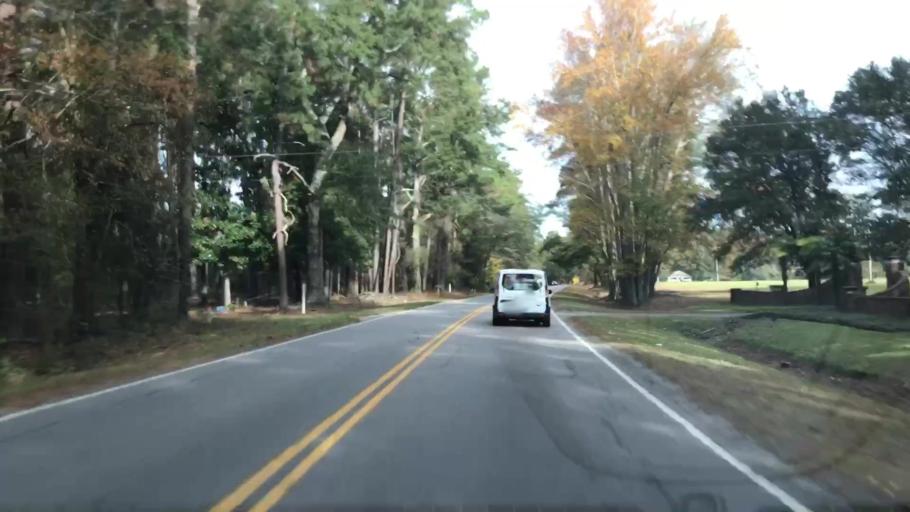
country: US
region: South Carolina
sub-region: Colleton County
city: Walterboro
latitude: 32.8771
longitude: -80.6177
